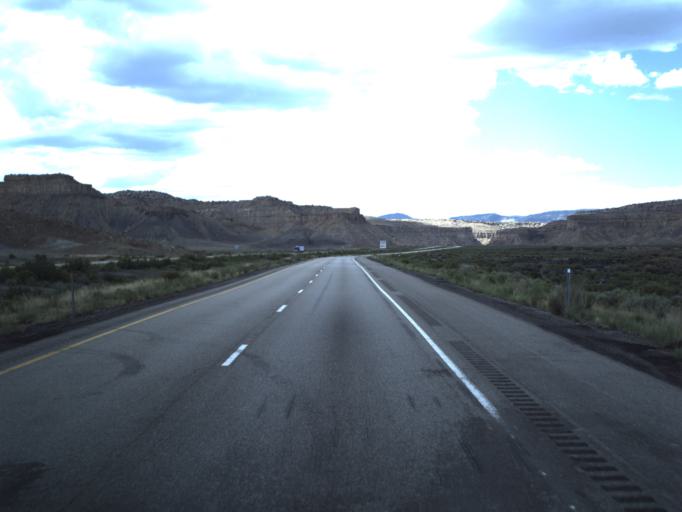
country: US
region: Utah
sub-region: Emery County
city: Ferron
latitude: 38.8103
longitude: -111.2236
